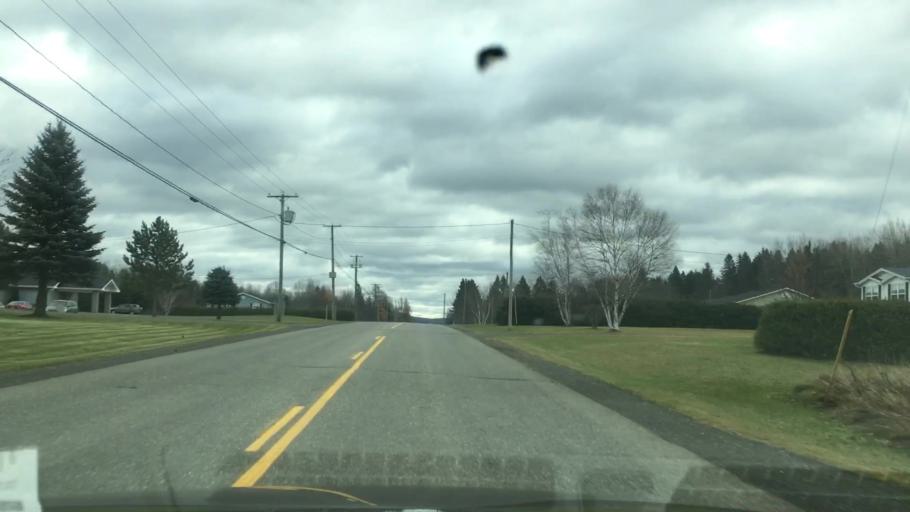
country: US
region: Maine
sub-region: Aroostook County
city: Fort Fairfield
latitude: 46.7567
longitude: -67.7658
